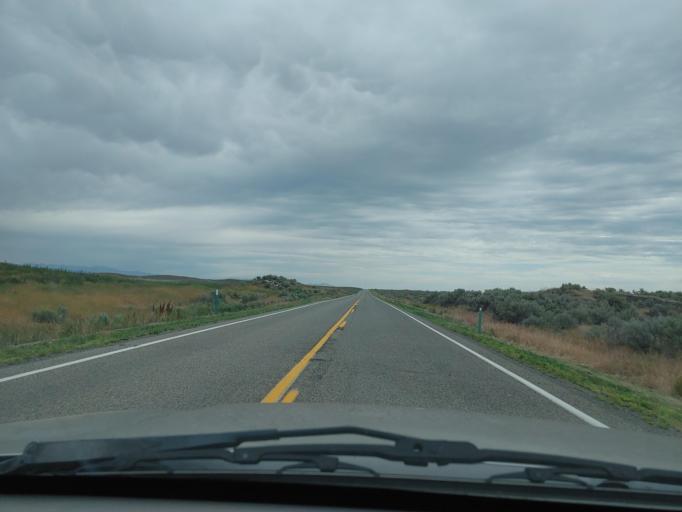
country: US
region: Idaho
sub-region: Lincoln County
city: Shoshone
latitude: 43.0661
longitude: -114.1191
